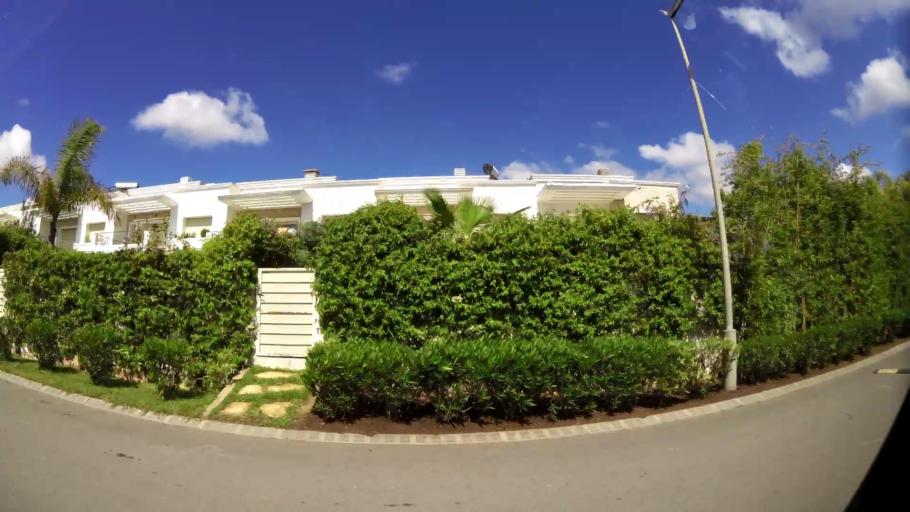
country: MA
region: Grand Casablanca
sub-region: Nouaceur
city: Bouskoura
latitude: 33.4691
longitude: -7.6089
